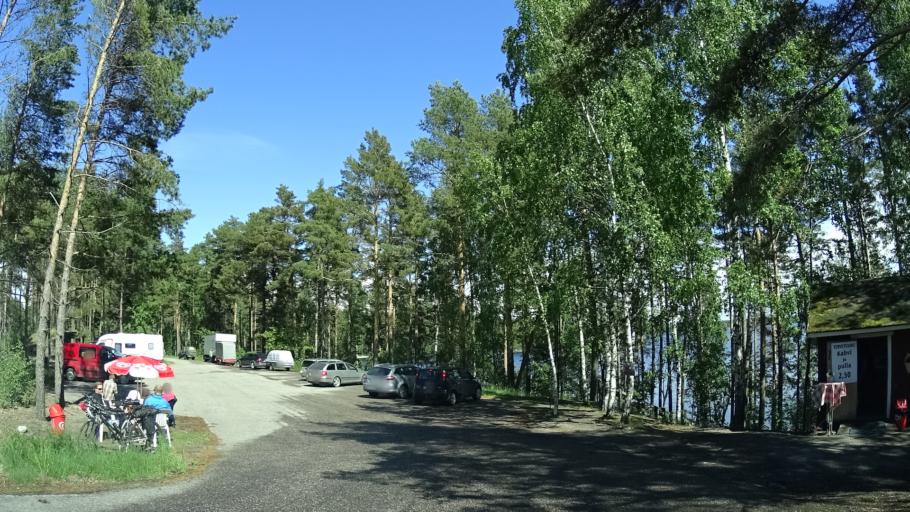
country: FI
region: Paijanne Tavastia
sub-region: Lahti
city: Asikkala
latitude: 61.2946
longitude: 25.5342
